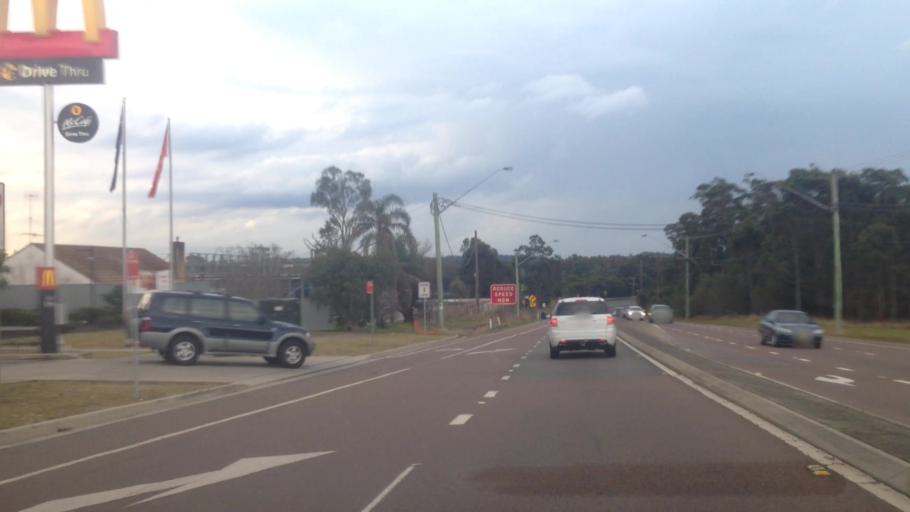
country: AU
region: New South Wales
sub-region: Wyong Shire
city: Tuggerawong
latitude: -33.2650
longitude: 151.4552
